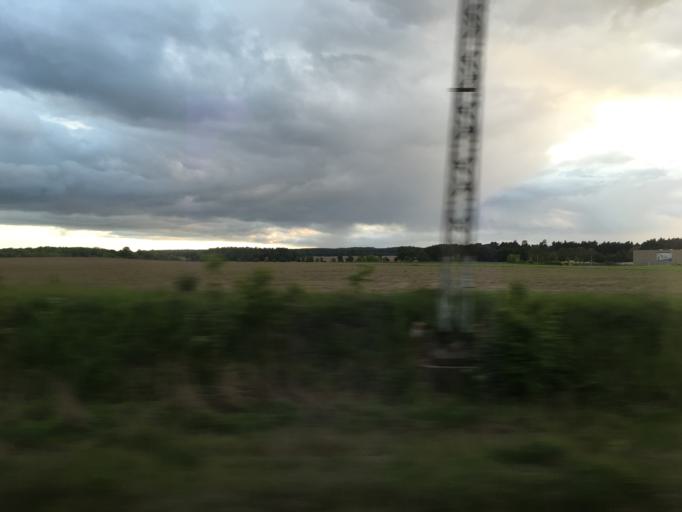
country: DE
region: Brandenburg
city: Golssen
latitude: 51.9816
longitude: 13.5711
